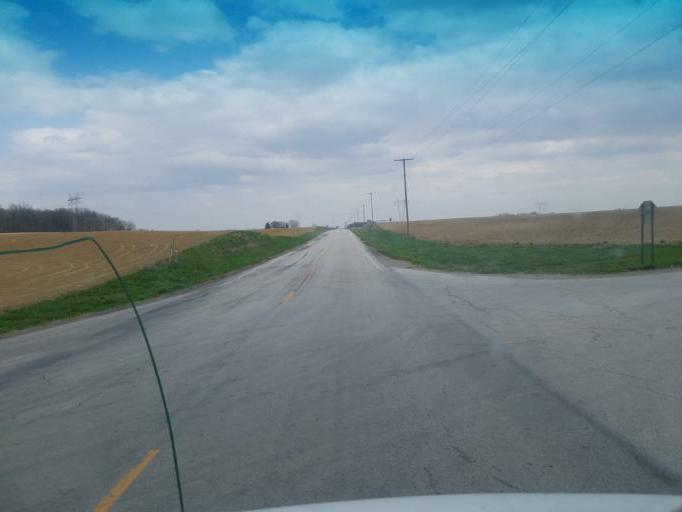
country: US
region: Ohio
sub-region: Wyandot County
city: Upper Sandusky
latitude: 40.9493
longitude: -83.2196
